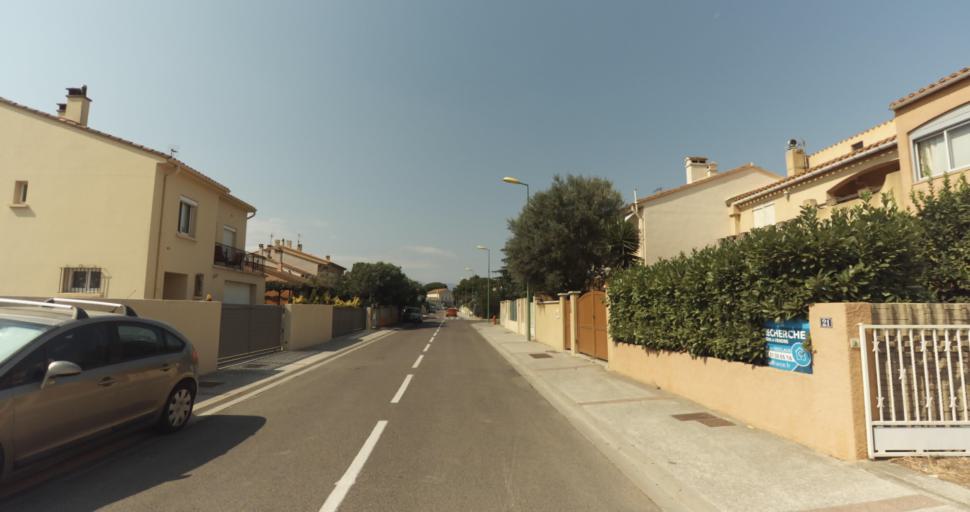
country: FR
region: Languedoc-Roussillon
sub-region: Departement des Pyrenees-Orientales
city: Latour-Bas-Elne
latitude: 42.6068
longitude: 3.0052
